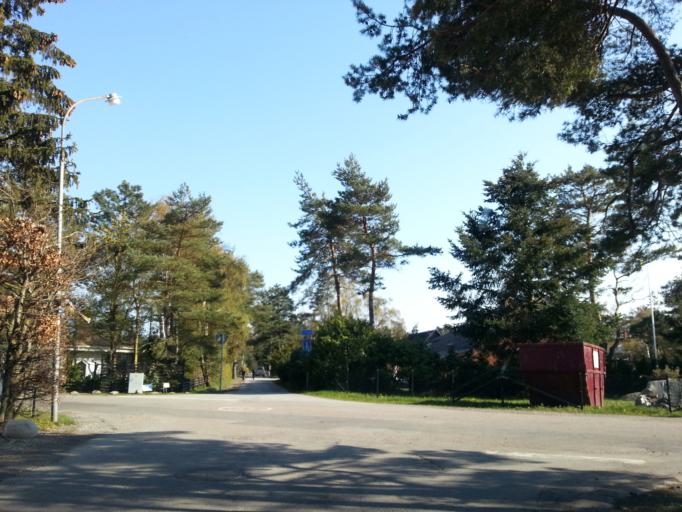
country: SE
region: Skane
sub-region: Vellinge Kommun
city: Hollviken
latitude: 55.4086
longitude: 12.9523
